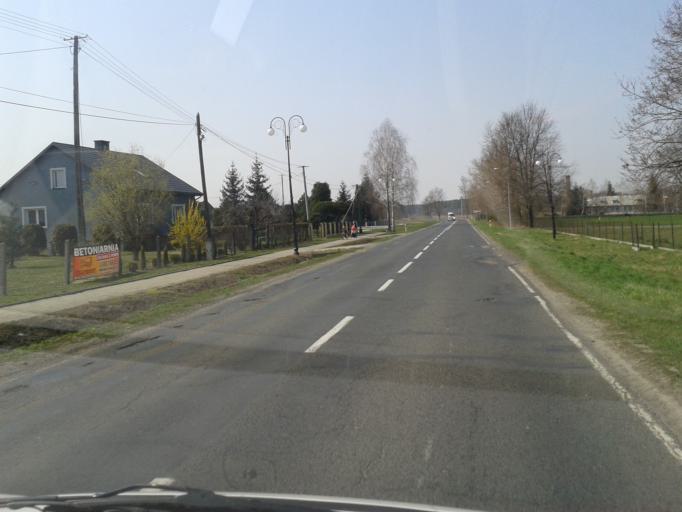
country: PL
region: Subcarpathian Voivodeship
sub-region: Powiat jaroslawski
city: Laszki
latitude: 50.0769
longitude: 22.8443
